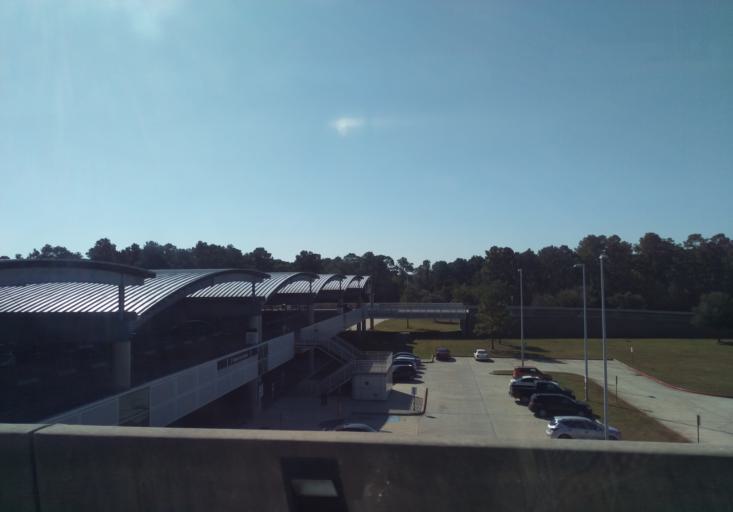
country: US
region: Texas
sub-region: Harris County
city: Aldine
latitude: 29.9696
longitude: -95.3340
